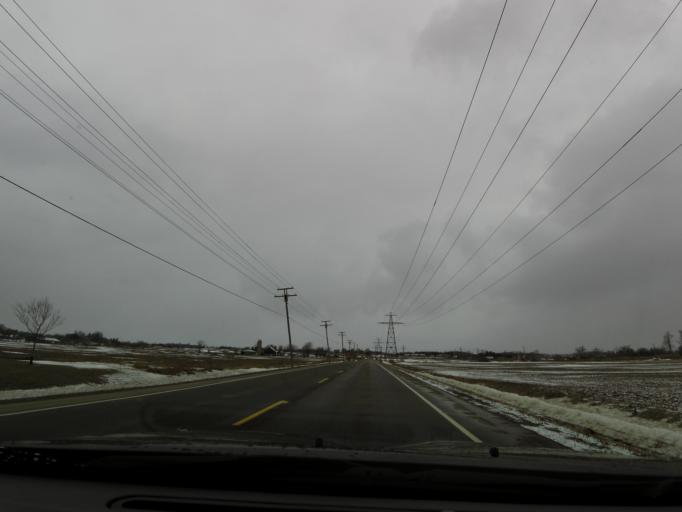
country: CA
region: Ontario
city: Ancaster
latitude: 43.2968
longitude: -79.9486
